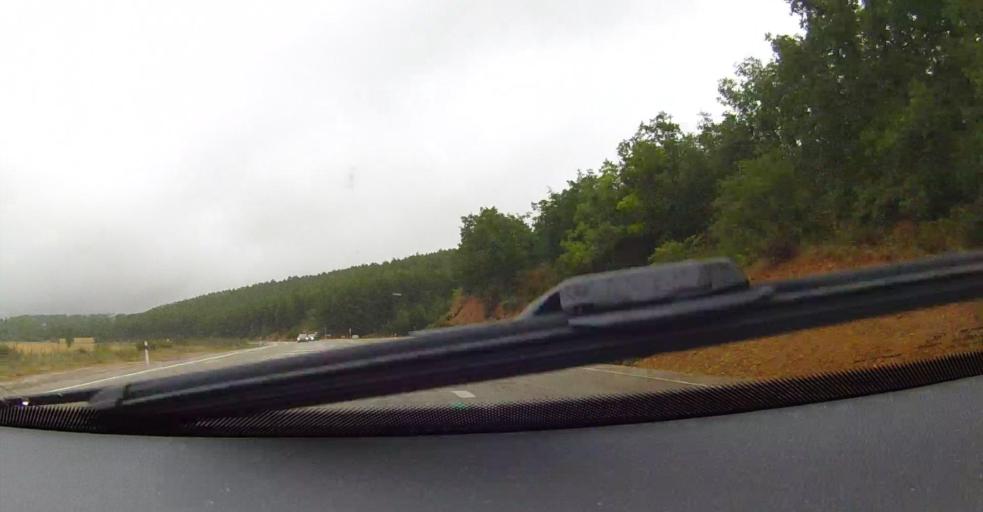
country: ES
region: Castille and Leon
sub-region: Provincia de Palencia
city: Saldana
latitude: 42.5489
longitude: -4.7328
